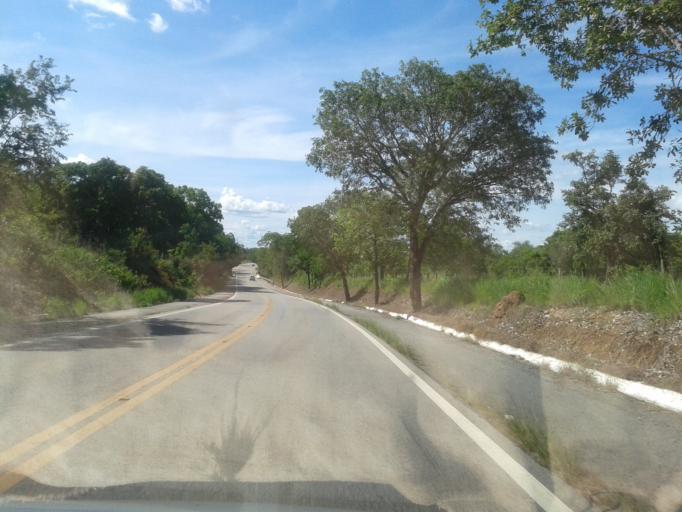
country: BR
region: Goias
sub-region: Itapuranga
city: Itapuranga
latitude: -15.3914
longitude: -50.3873
